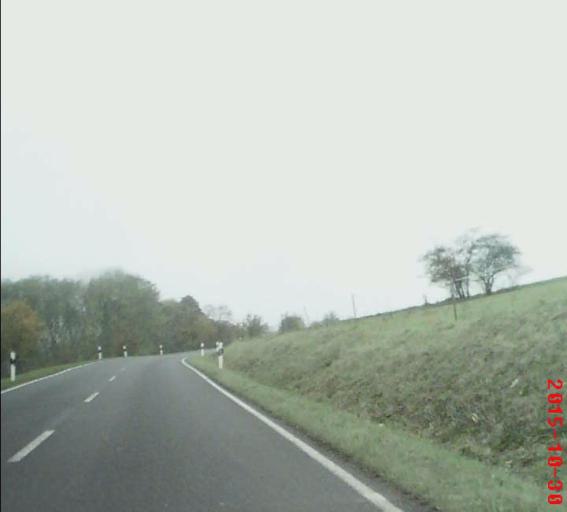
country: DE
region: Thuringia
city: Buttstedt
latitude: 51.2659
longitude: 10.2951
